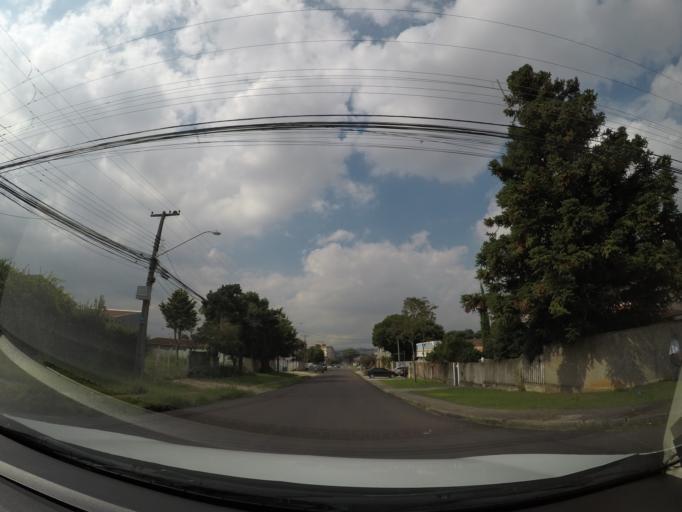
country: BR
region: Parana
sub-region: Curitiba
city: Curitiba
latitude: -25.4876
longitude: -49.2582
